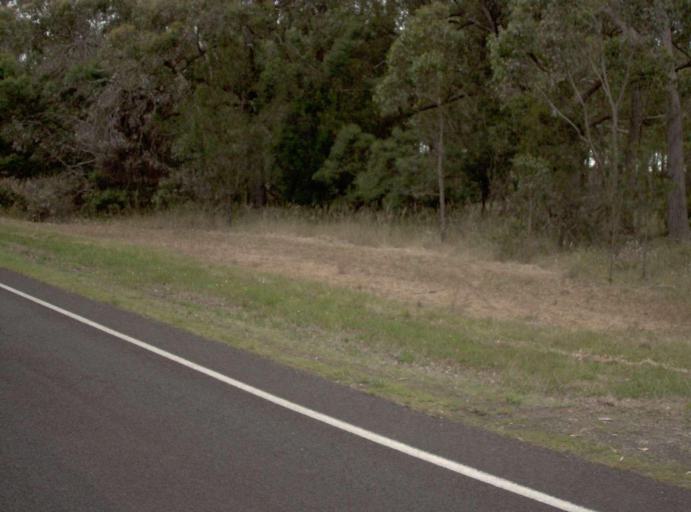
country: AU
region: Victoria
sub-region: Wellington
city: Sale
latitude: -38.3609
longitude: 146.9923
